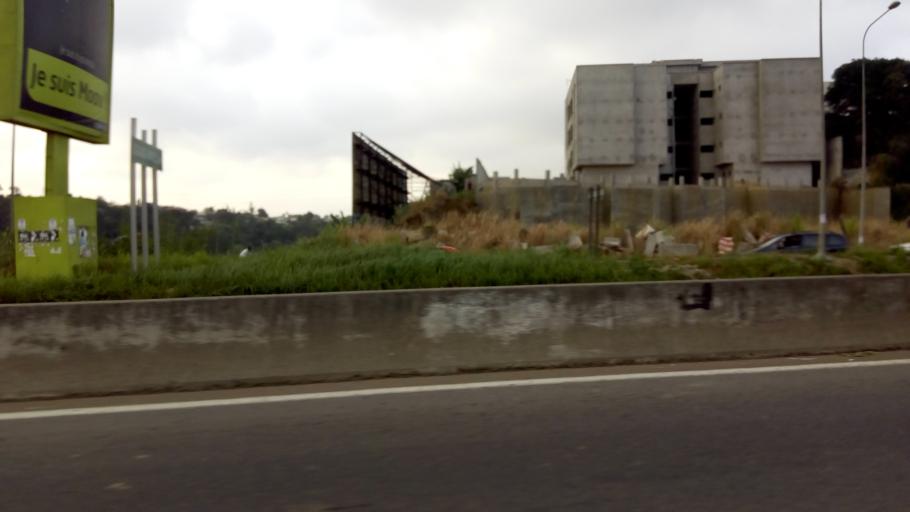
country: CI
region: Lagunes
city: Abidjan
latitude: 5.3522
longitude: -3.9818
